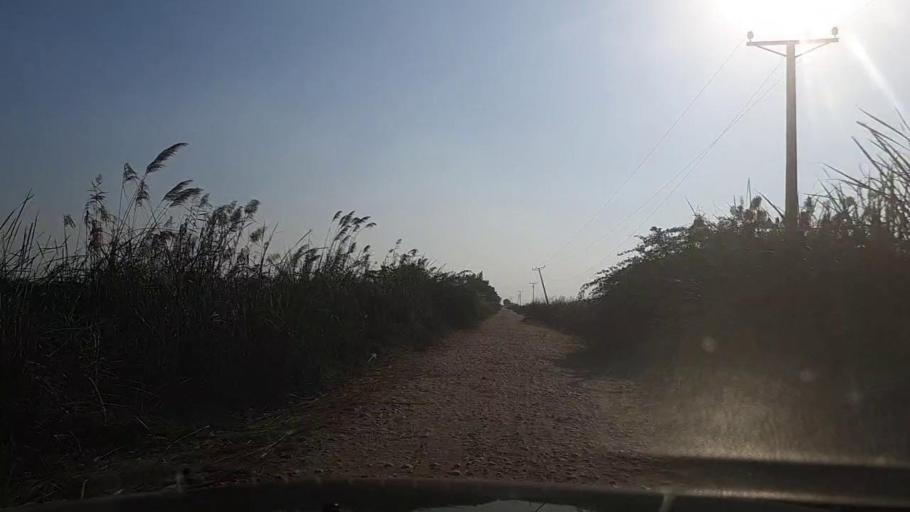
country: PK
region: Sindh
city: Gharo
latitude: 24.7246
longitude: 67.6930
